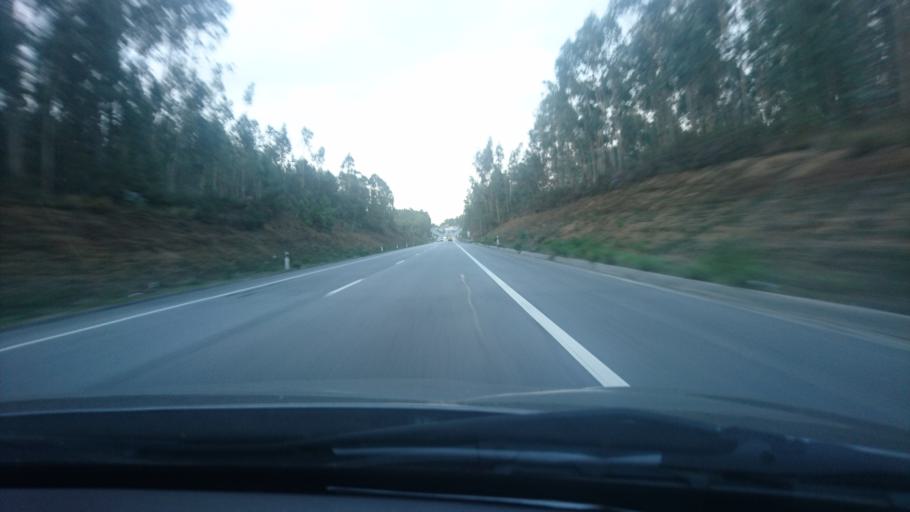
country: PT
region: Aveiro
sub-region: Santa Maria da Feira
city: Milheiros de Poiares
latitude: 40.9304
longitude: -8.4816
